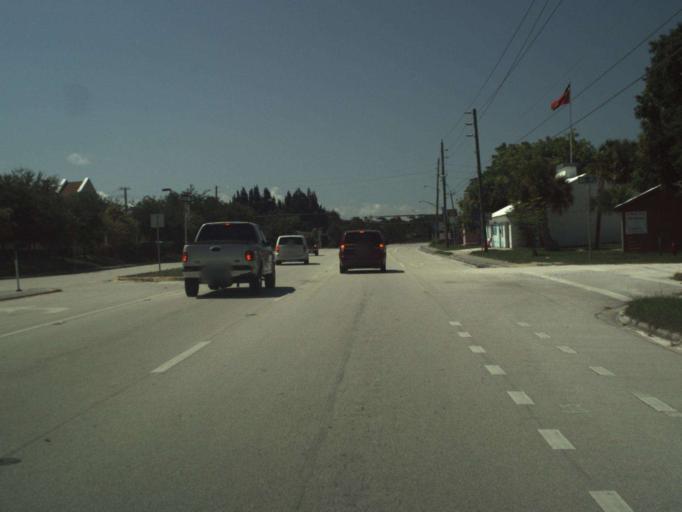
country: US
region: Florida
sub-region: Indian River County
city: Winter Beach
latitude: 27.7471
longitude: -80.4345
